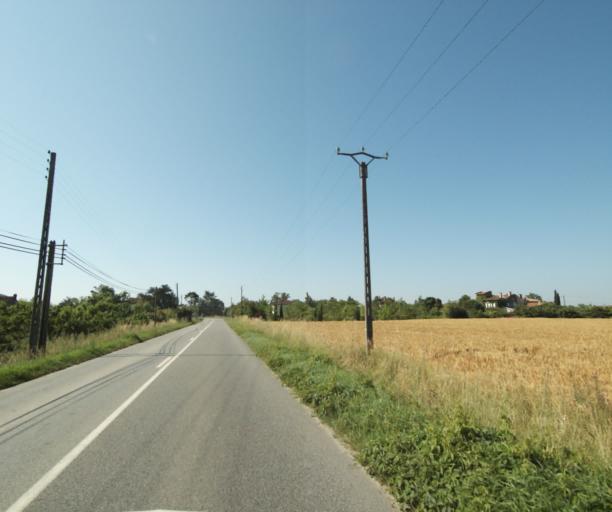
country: FR
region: Midi-Pyrenees
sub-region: Departement du Tarn-et-Garonne
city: Bressols
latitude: 43.9898
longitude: 1.3512
